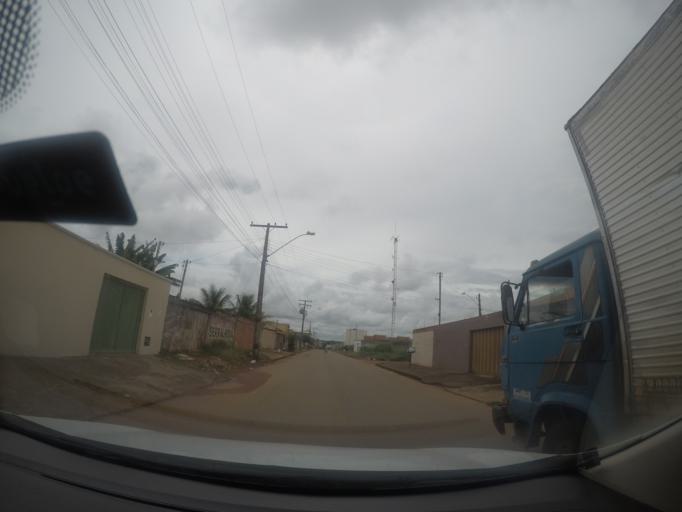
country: BR
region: Goias
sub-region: Trindade
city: Trindade
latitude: -16.6908
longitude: -49.4051
